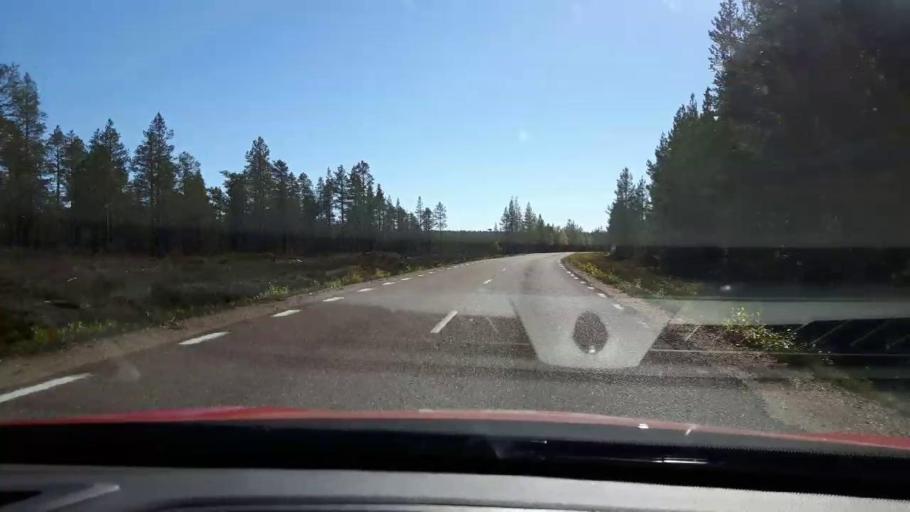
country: SE
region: Jaemtland
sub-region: Harjedalens Kommun
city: Sveg
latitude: 61.7409
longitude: 14.1616
